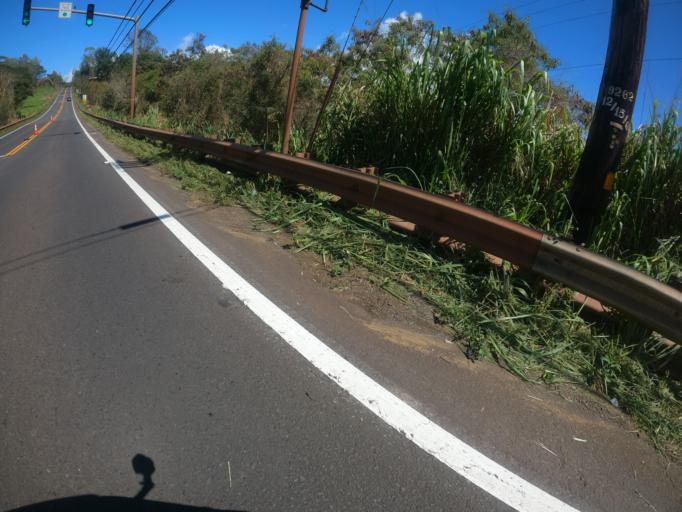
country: US
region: Hawaii
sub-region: Honolulu County
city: Schofield Barracks
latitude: 21.4759
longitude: -158.0509
